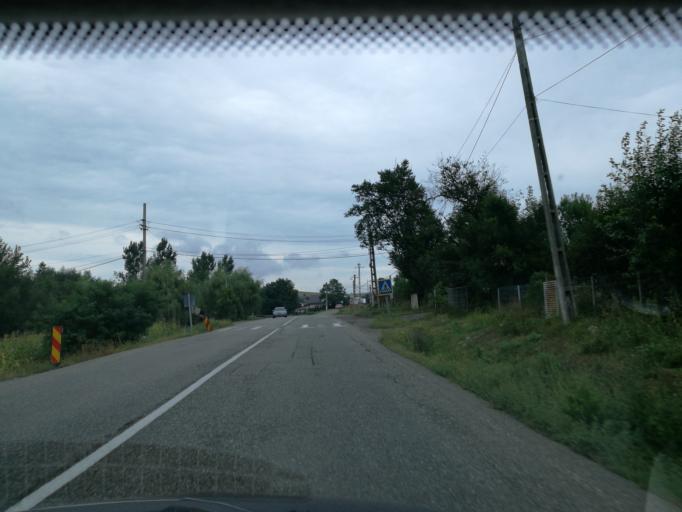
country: RO
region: Suceava
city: Bunesti-Regat
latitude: 47.5190
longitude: 26.2855
